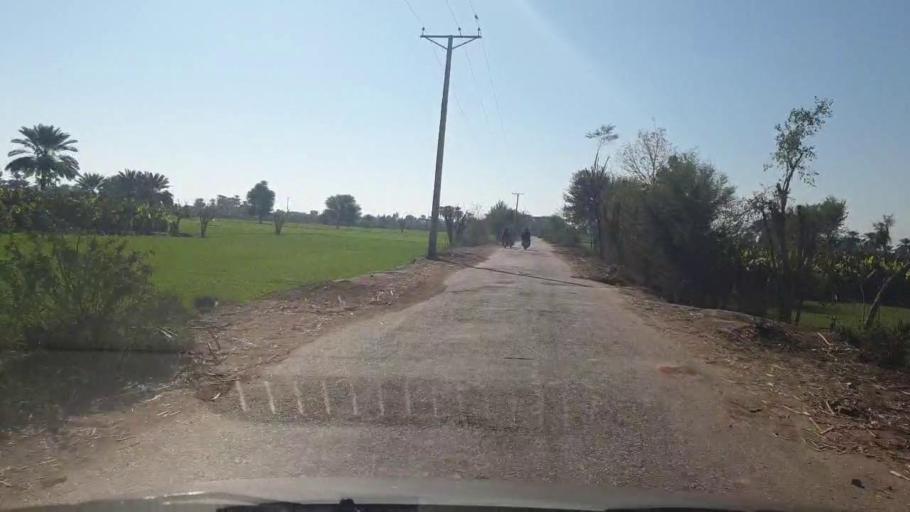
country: PK
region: Sindh
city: Bozdar
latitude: 27.2527
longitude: 68.6521
